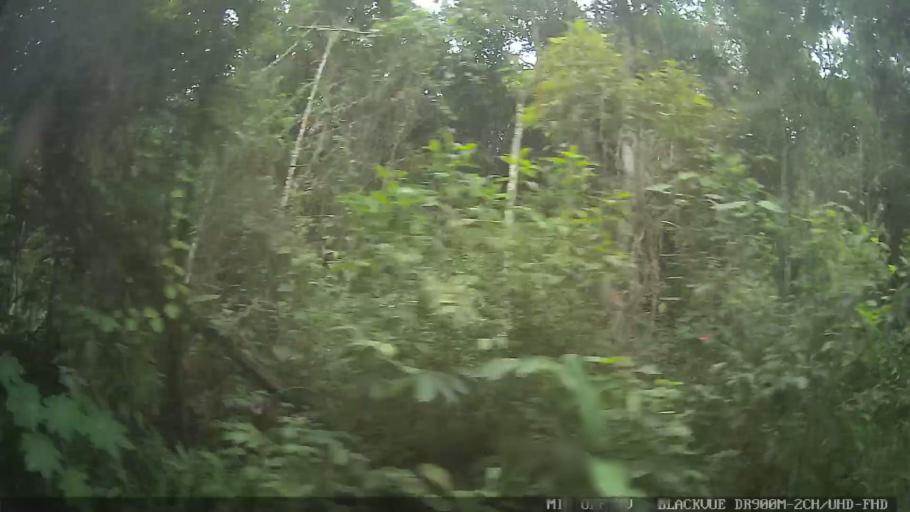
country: BR
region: Sao Paulo
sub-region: Bom Jesus Dos Perdoes
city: Bom Jesus dos Perdoes
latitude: -23.1499
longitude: -46.5090
